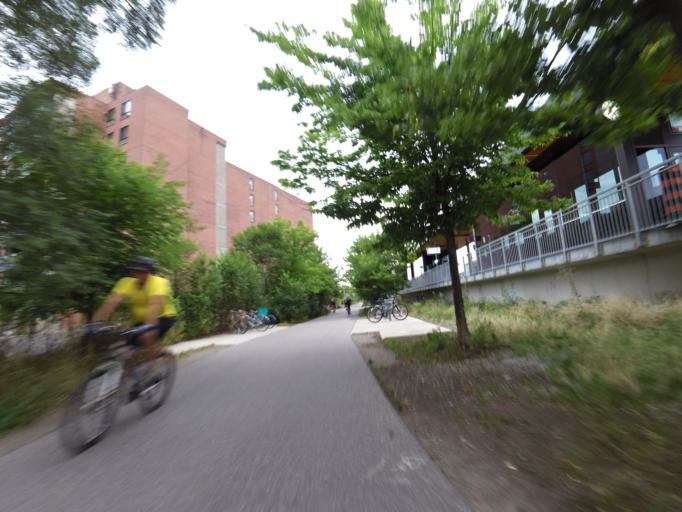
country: CA
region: Ontario
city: Toronto
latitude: 43.6576
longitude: -79.4503
